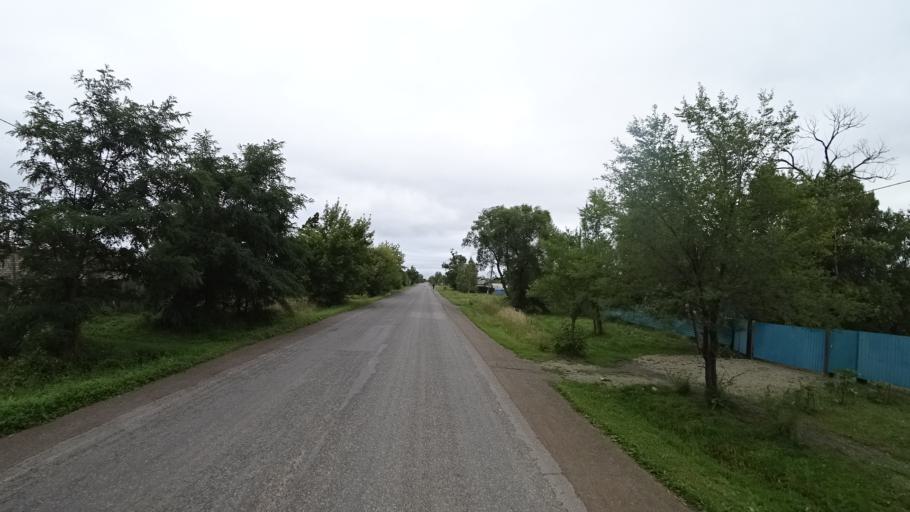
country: RU
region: Primorskiy
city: Chernigovka
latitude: 44.3278
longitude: 132.6020
